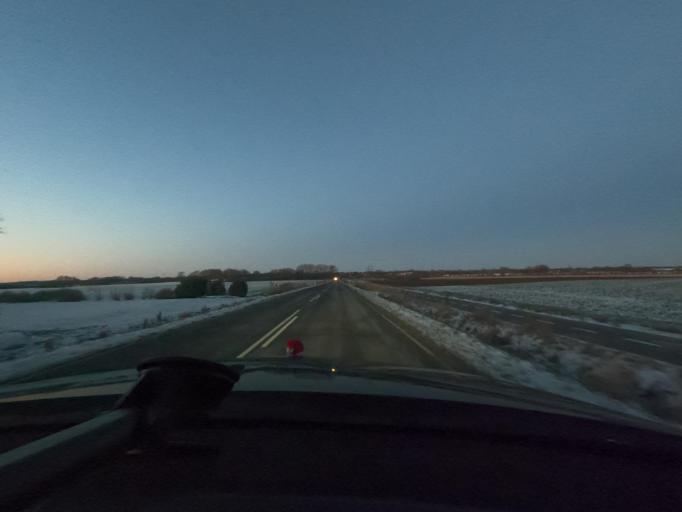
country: DK
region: South Denmark
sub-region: Sonderborg Kommune
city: Horuphav
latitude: 54.8685
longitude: 9.9964
